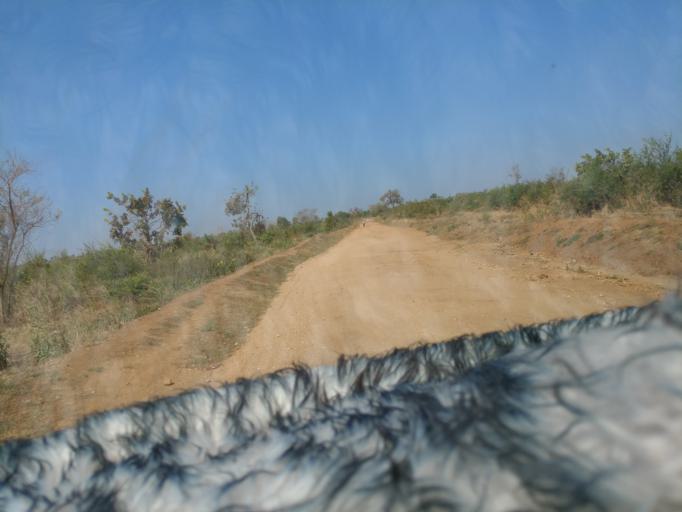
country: UG
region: Northern Region
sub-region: Yumbe District
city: Yumbe
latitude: 3.3923
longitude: 31.3428
